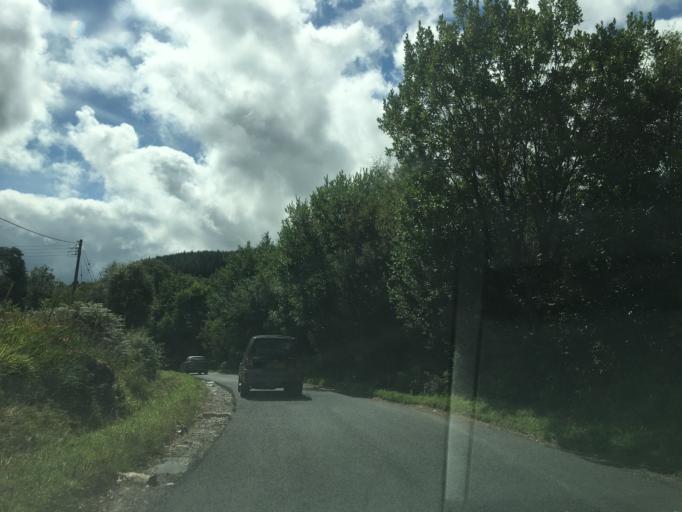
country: GB
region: Scotland
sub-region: Argyll and Bute
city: Tarbert
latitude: 55.9048
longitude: -5.2403
